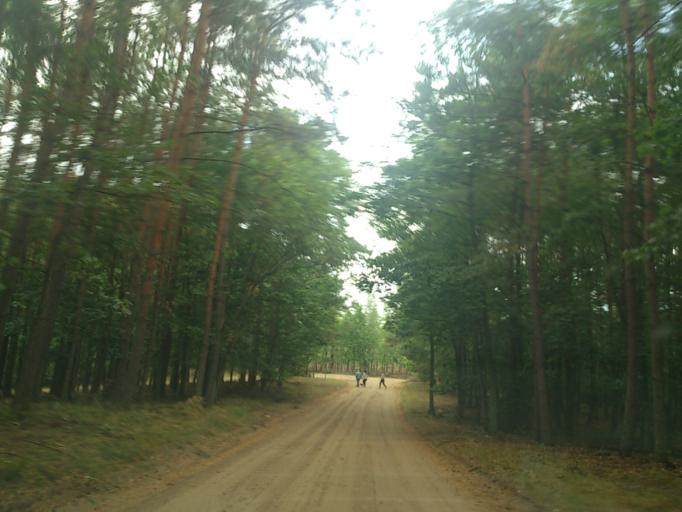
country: PL
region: Greater Poland Voivodeship
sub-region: Powiat poznanski
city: Kobylnica
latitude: 52.5319
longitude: 17.1156
